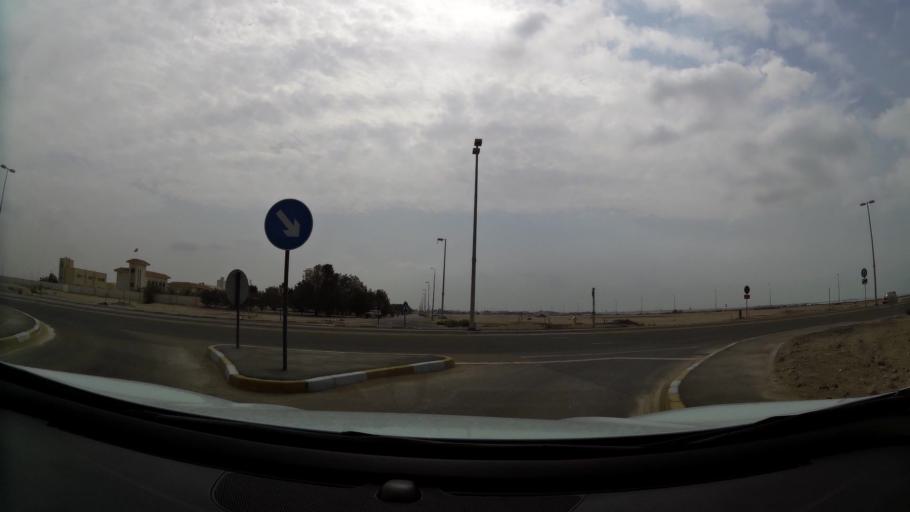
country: AE
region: Abu Dhabi
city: Abu Dhabi
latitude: 24.6065
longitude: 54.6445
